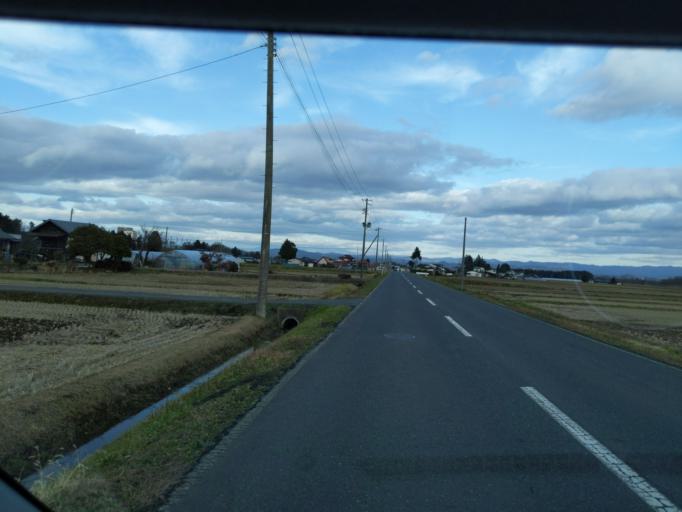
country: JP
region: Iwate
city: Mizusawa
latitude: 39.1696
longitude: 141.0876
